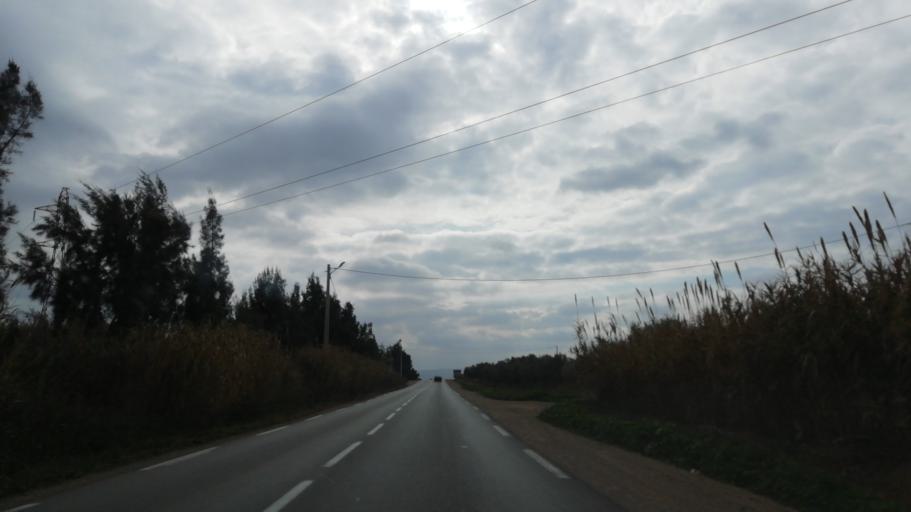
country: DZ
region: Oran
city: Sidi ech Chahmi
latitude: 35.5731
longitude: -0.4509
